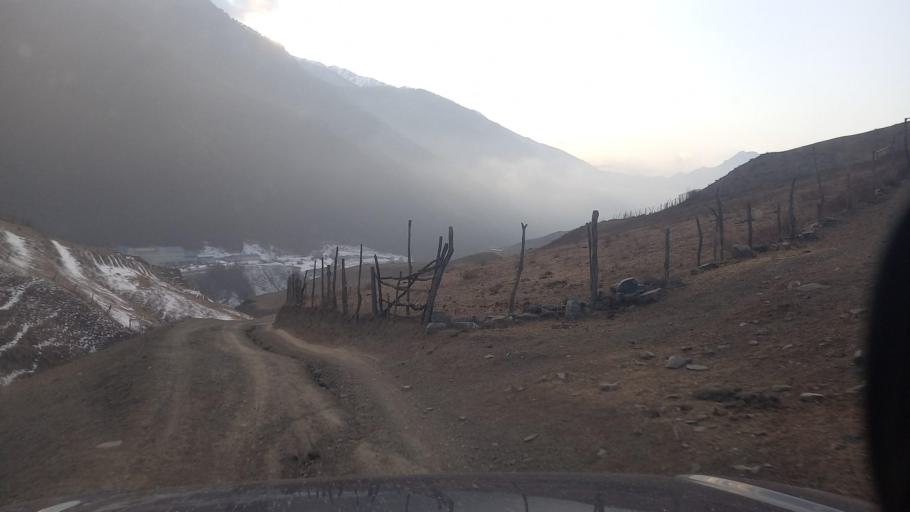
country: RU
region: Ingushetiya
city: Dzhayrakh
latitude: 42.8048
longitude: 44.7592
